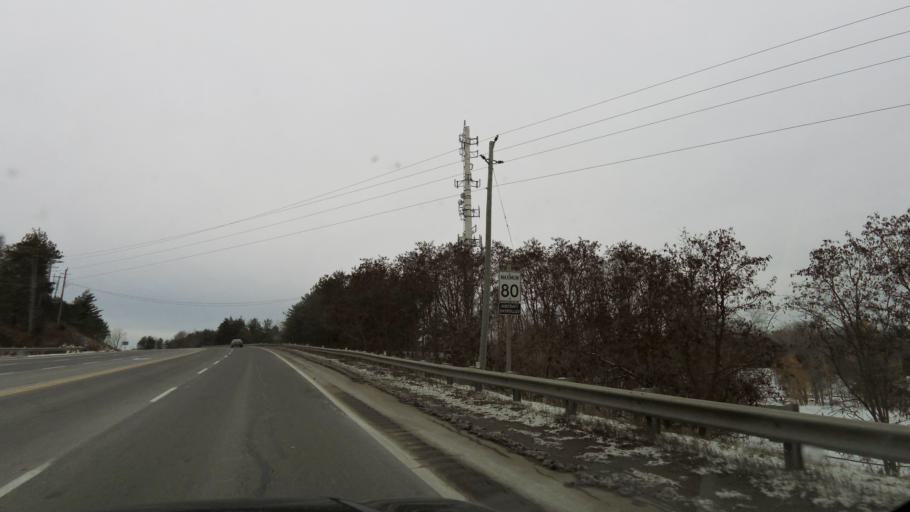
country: CA
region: Ontario
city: Newmarket
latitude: 44.0434
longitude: -79.5308
